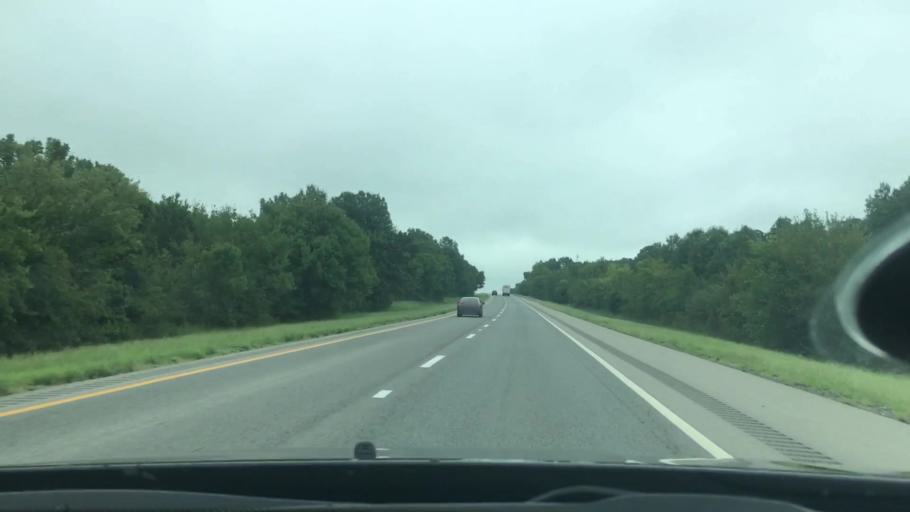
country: US
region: Oklahoma
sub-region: Muskogee County
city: Warner
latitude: 35.4563
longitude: -95.3935
